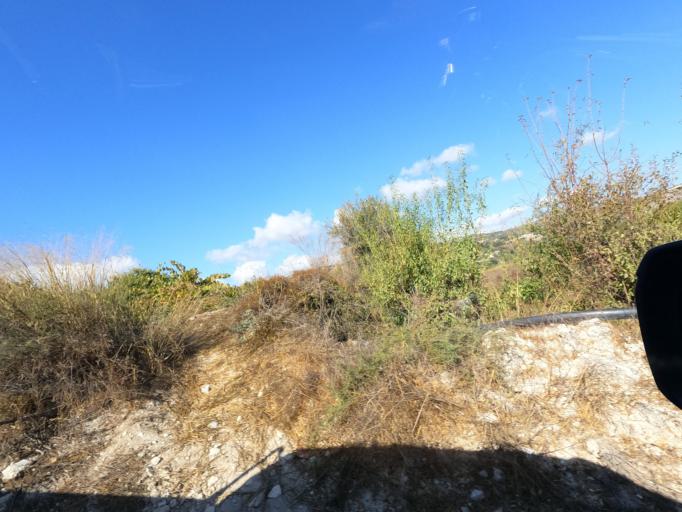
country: CY
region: Pafos
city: Mesogi
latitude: 34.8488
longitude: 32.5224
